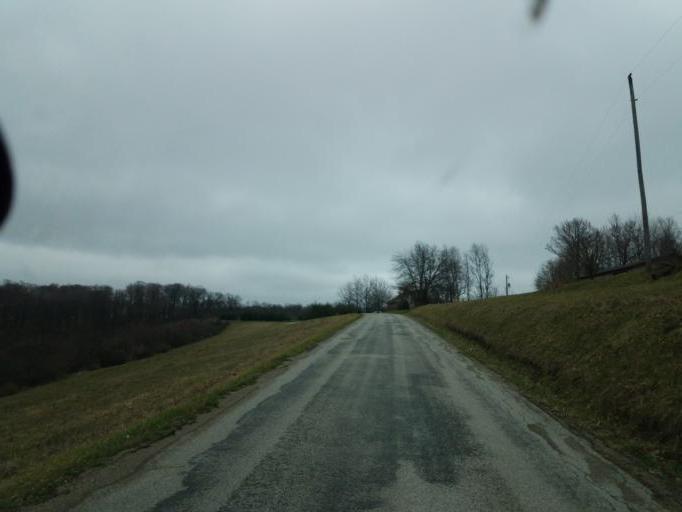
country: US
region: Ohio
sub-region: Sandusky County
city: Bellville
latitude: 40.5906
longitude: -82.4751
